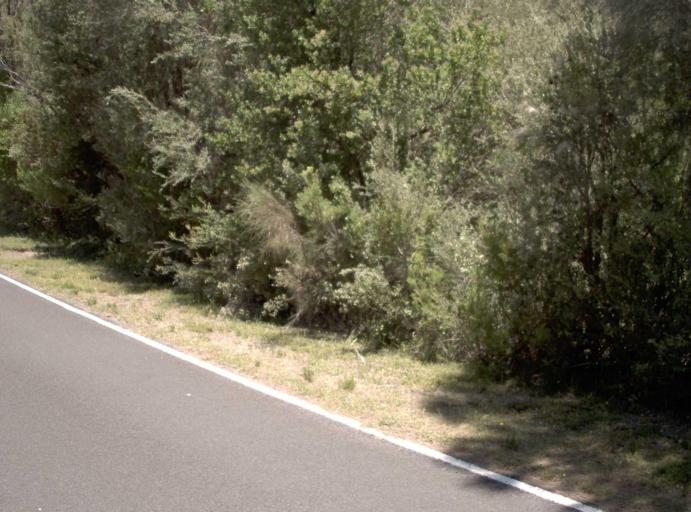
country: AU
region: Victoria
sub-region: Latrobe
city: Morwell
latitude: -38.8734
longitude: 146.2668
